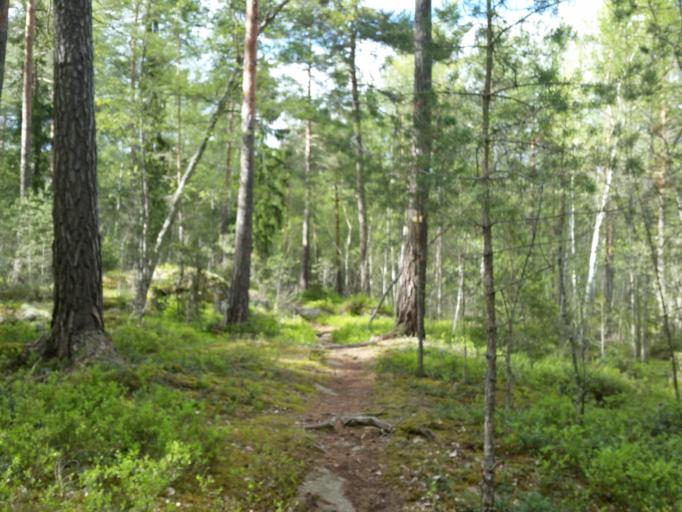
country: SE
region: Stockholm
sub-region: Sollentuna Kommun
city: Sollentuna
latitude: 59.4649
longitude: 17.9530
